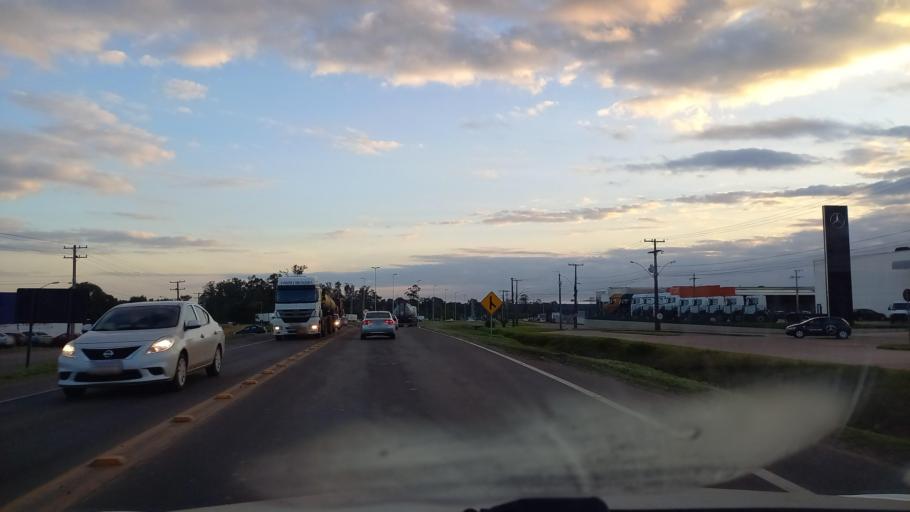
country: BR
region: Rio Grande do Sul
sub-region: Santa Cruz Do Sul
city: Santa Cruz do Sul
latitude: -29.6878
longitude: -52.4473
